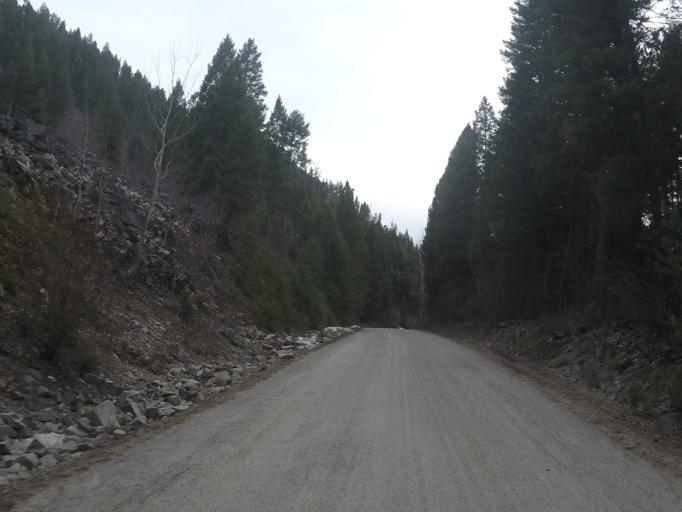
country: US
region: Montana
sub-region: Ravalli County
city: Hamilton
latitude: 45.8453
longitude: -114.0354
